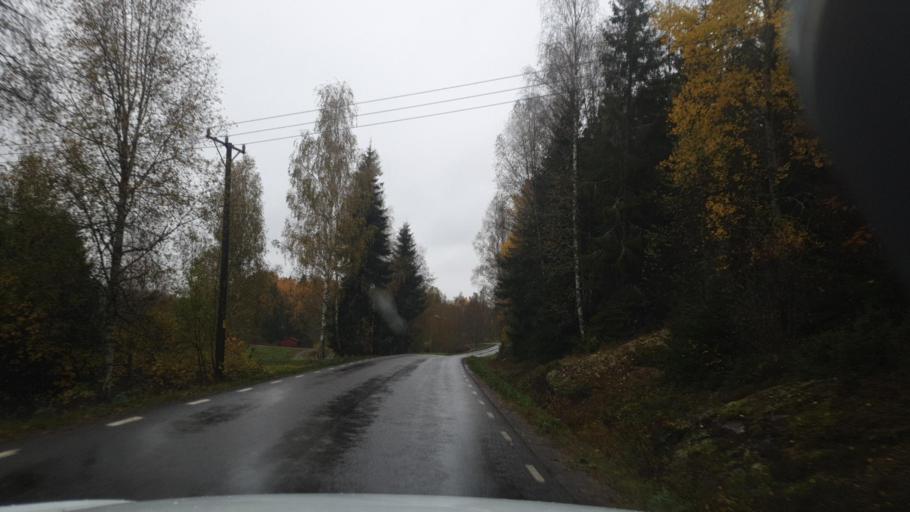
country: SE
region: Vaermland
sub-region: Eda Kommun
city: Charlottenberg
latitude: 59.8022
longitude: 12.1537
